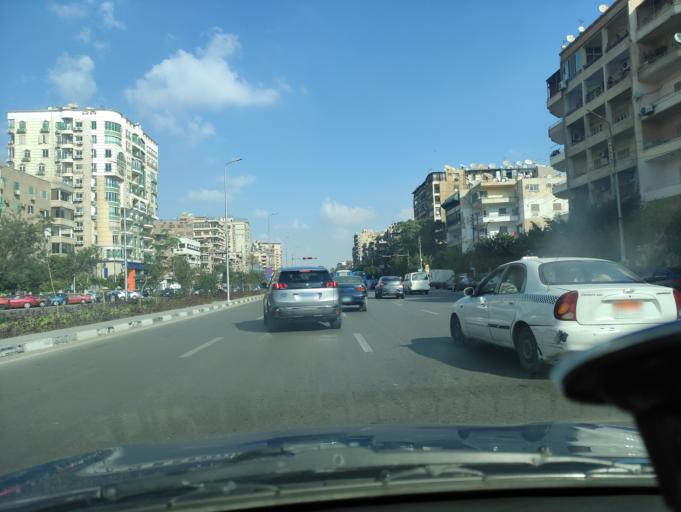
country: EG
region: Muhafazat al Qahirah
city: Cairo
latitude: 30.1008
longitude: 31.3440
